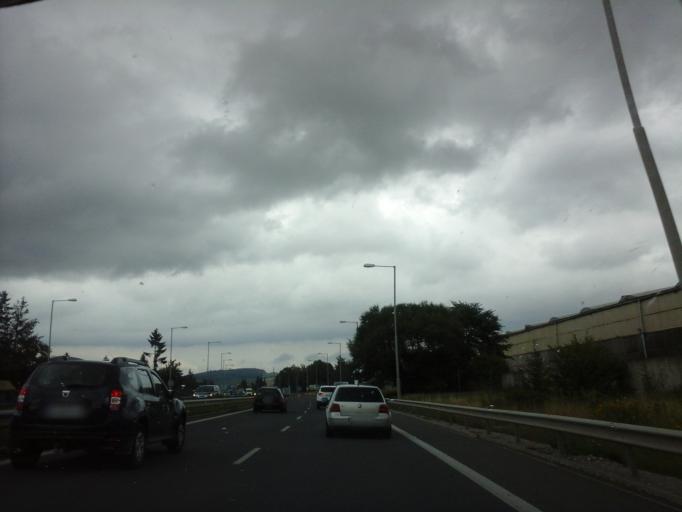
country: SK
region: Presovsky
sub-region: Okres Poprad
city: Poprad
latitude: 49.0640
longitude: 20.3193
